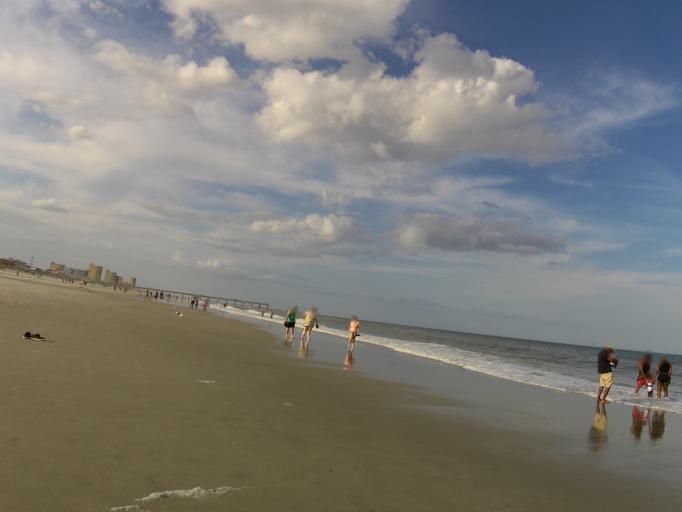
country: US
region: Florida
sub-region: Duval County
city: Jacksonville Beach
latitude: 30.2868
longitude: -81.3868
